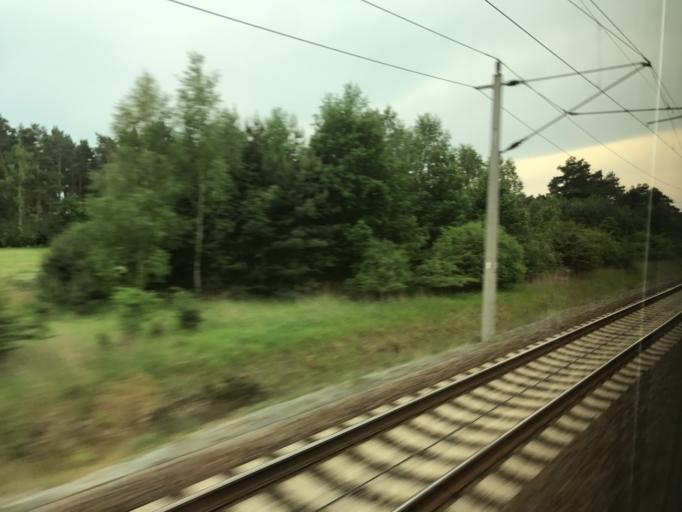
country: DE
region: Saxony-Anhalt
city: Mieste
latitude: 52.4741
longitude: 11.1613
